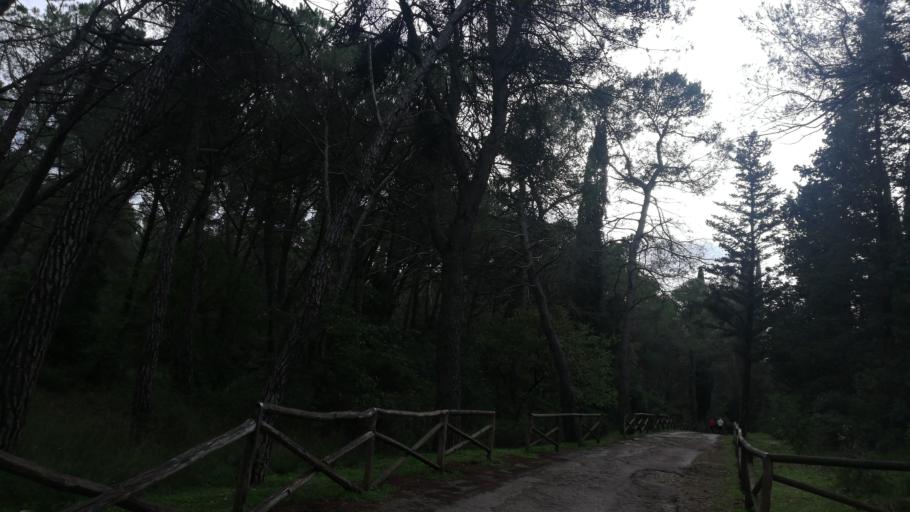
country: IT
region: Apulia
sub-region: Provincia di Bari
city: Cassano delle Murge
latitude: 40.8891
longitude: 16.7005
